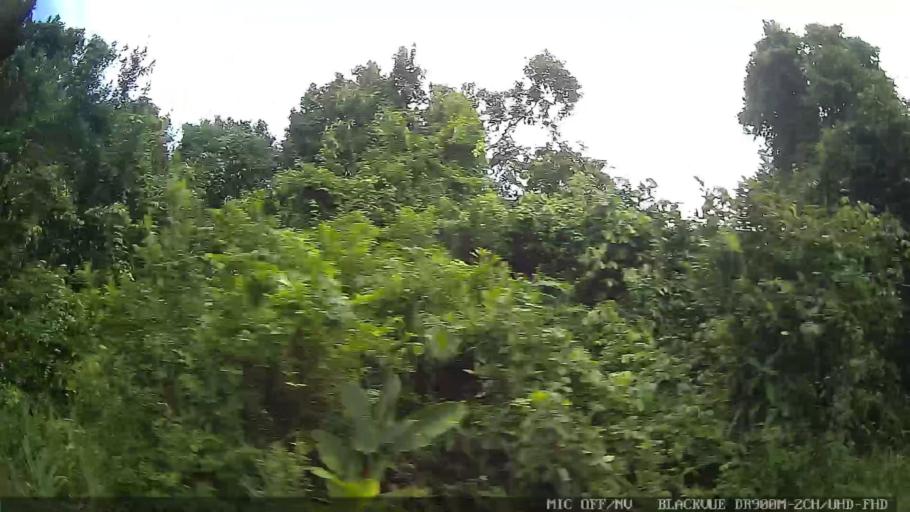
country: BR
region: Sao Paulo
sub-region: Iguape
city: Iguape
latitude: -24.6621
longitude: -47.4189
